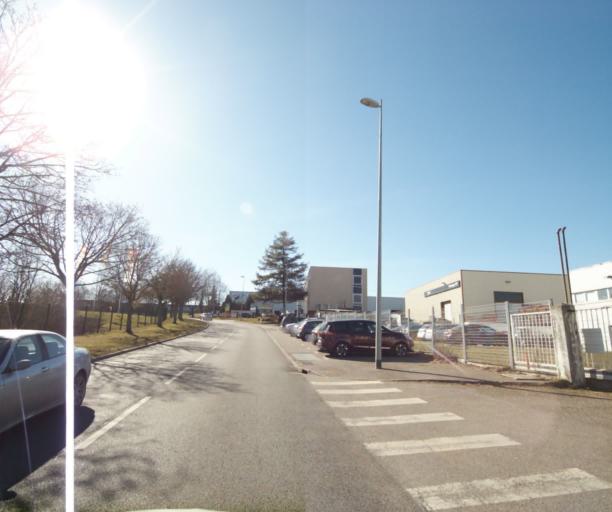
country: FR
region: Lorraine
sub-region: Departement de Meurthe-et-Moselle
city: Richardmenil
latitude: 48.6148
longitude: 6.1812
